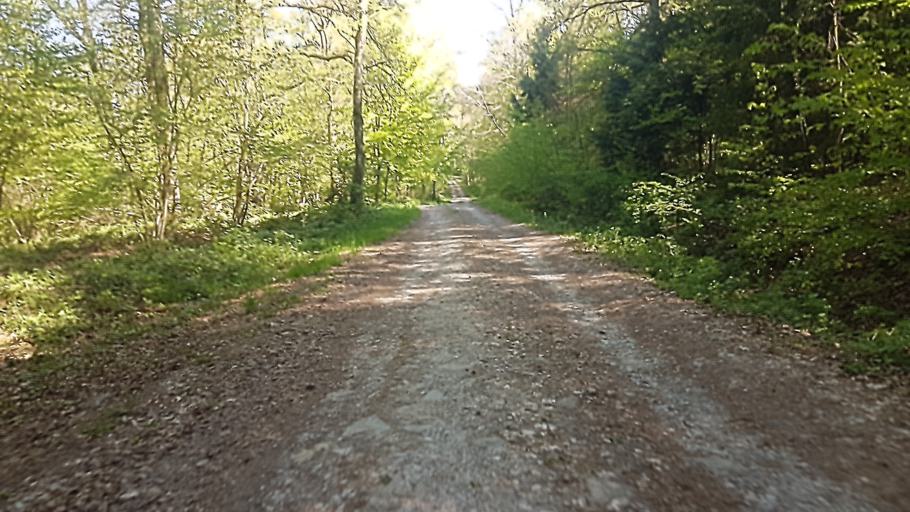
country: BE
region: Wallonia
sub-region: Province de Namur
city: Couvin
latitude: 50.0615
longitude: 4.5878
